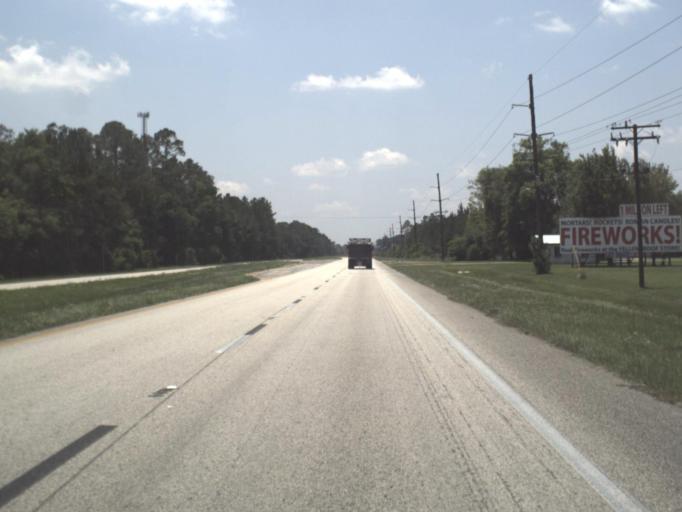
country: US
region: Florida
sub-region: Bradford County
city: Starke
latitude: 30.0170
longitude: -82.0866
